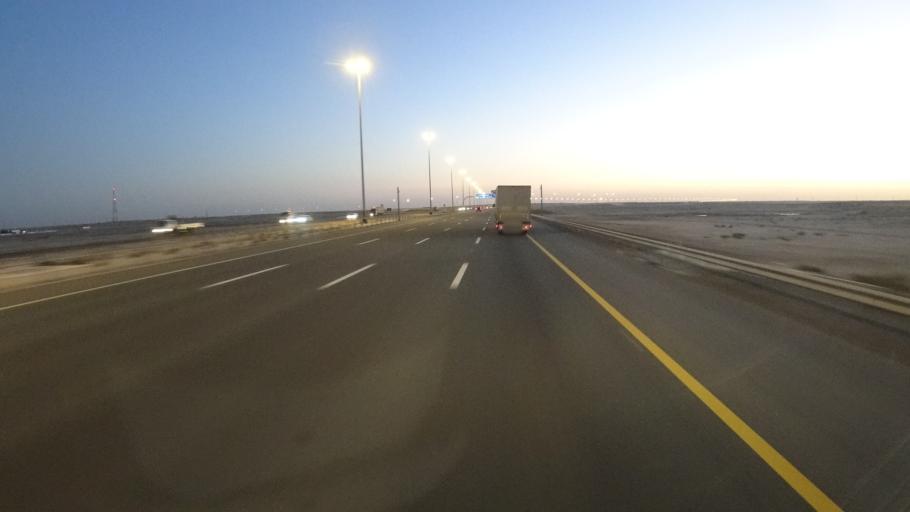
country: AE
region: Dubai
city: Dubai
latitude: 24.7764
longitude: 54.9541
